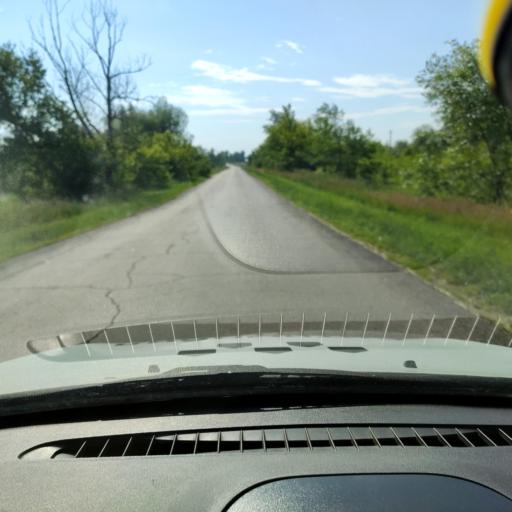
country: RU
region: Samara
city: Zhigulevsk
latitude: 53.3534
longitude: 49.3353
